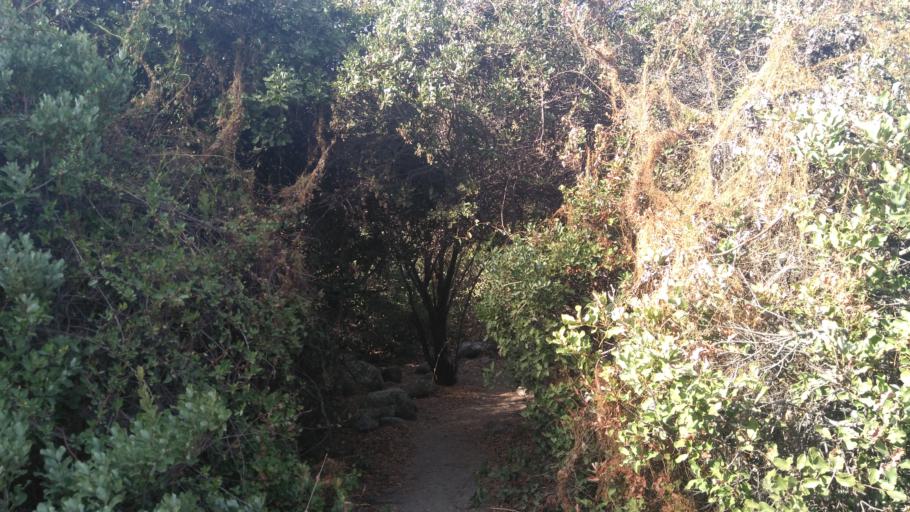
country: CL
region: Santiago Metropolitan
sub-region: Provincia de Cordillera
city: Puente Alto
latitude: -33.7252
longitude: -70.4830
